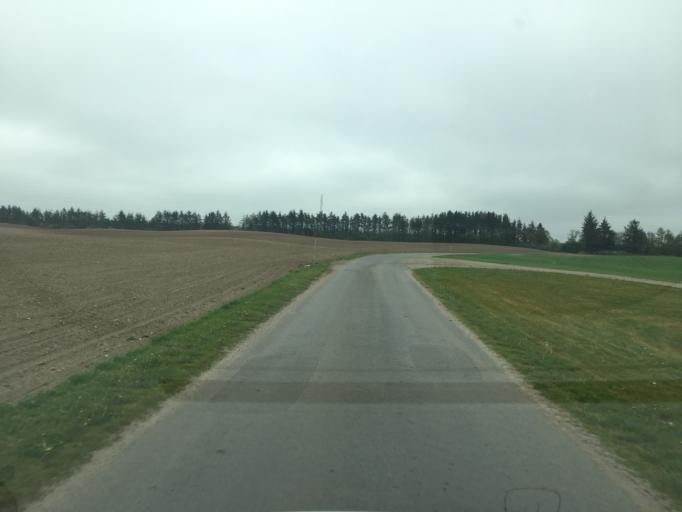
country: DK
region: South Denmark
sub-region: Aabenraa Kommune
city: Krusa
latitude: 54.8841
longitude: 9.4029
